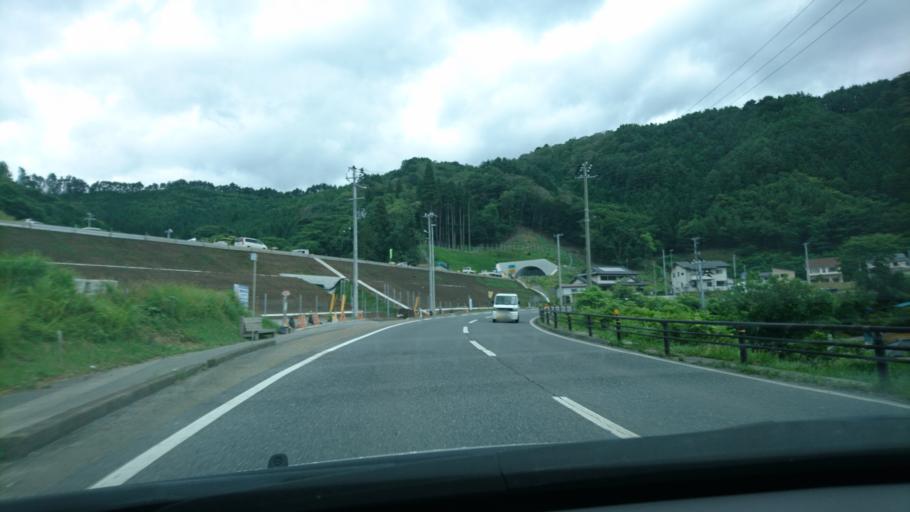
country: JP
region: Iwate
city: Kamaishi
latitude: 39.2102
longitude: 141.8645
